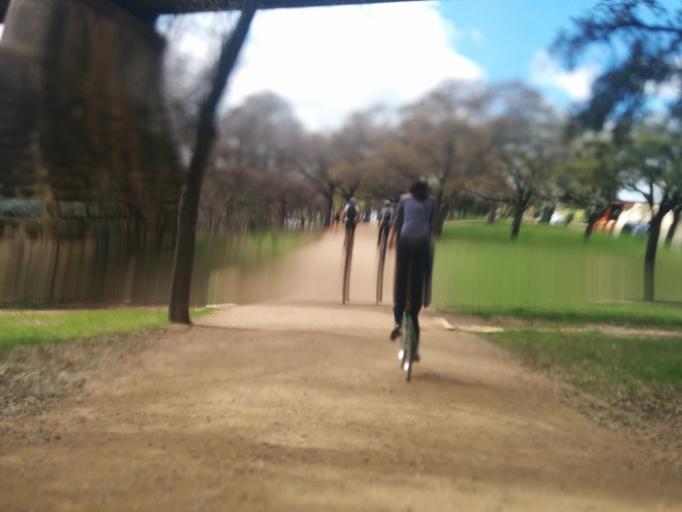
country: US
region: Texas
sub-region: Travis County
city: Austin
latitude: 30.2658
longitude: -97.7538
